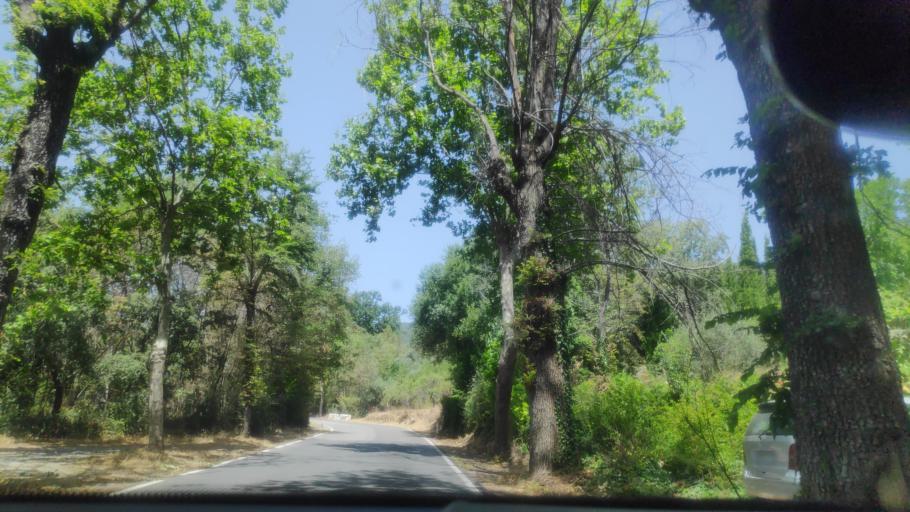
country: ES
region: Andalusia
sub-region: Provincia de Granada
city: Portugos
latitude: 36.9400
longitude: -3.3038
